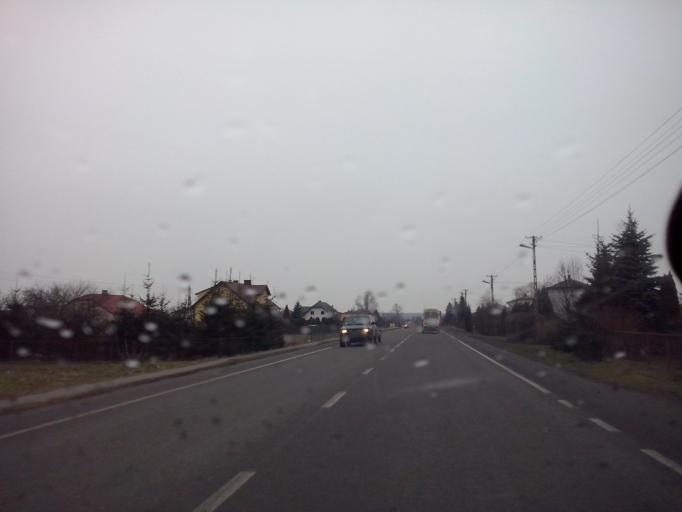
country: PL
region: Lublin Voivodeship
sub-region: Powiat zamojski
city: Michalow
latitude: 50.7163
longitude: 23.0341
